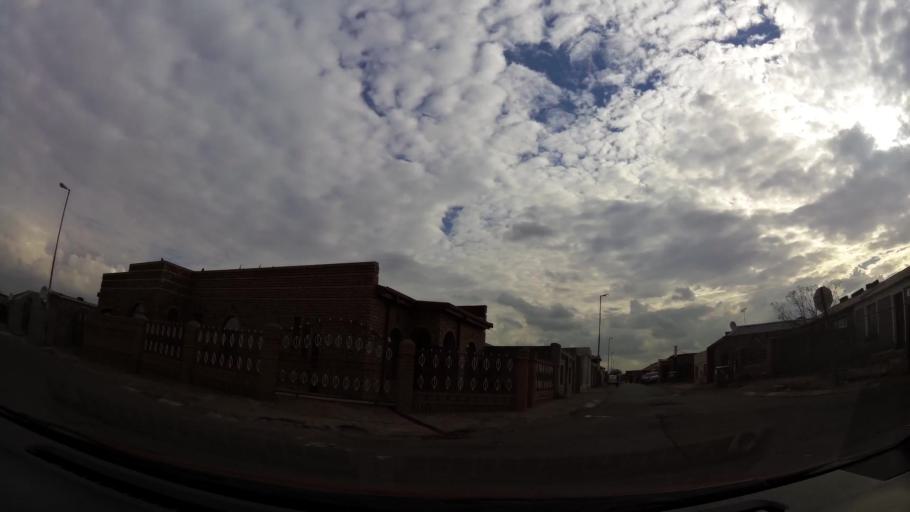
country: ZA
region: Gauteng
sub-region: City of Johannesburg Metropolitan Municipality
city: Soweto
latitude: -26.2467
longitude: 27.8343
